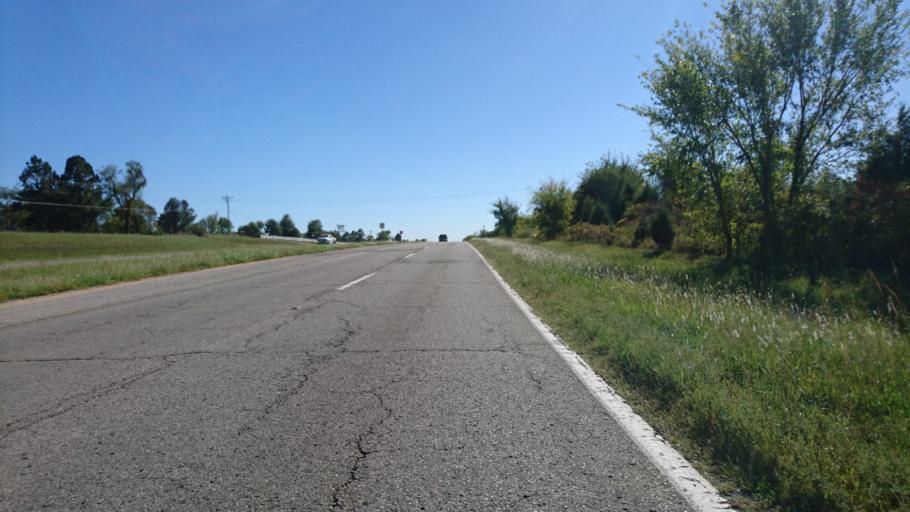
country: US
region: Oklahoma
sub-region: Rogers County
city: Bushyhead
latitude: 36.4166
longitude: -95.5360
